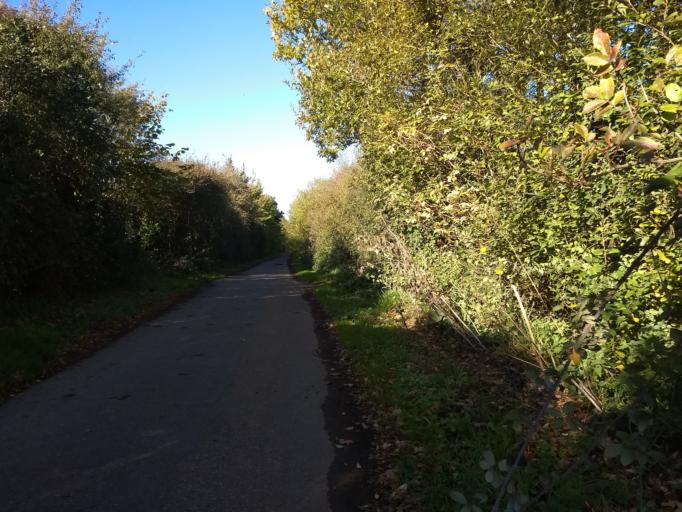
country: GB
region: England
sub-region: Isle of Wight
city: Newchurch
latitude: 50.6601
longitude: -1.2591
